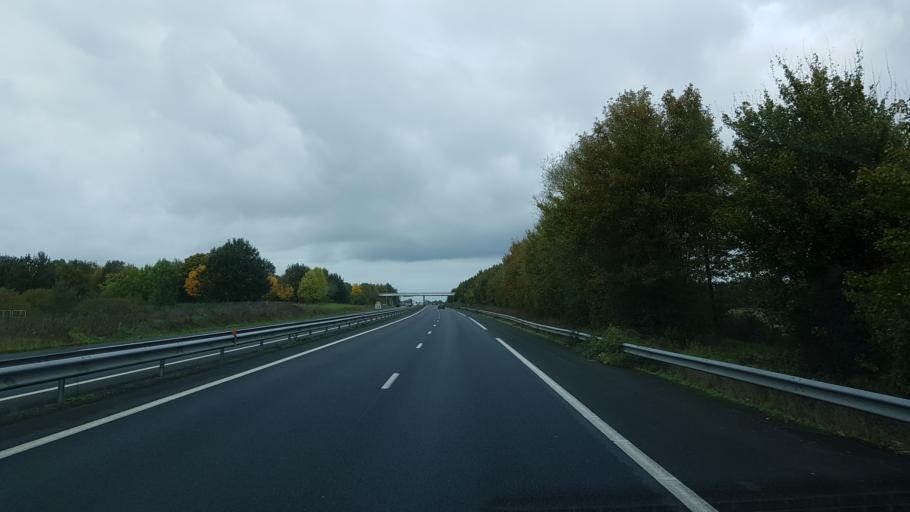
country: FR
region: Pays de la Loire
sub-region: Departement de la Vendee
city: Les Brouzils
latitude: 46.8810
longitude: -1.2890
